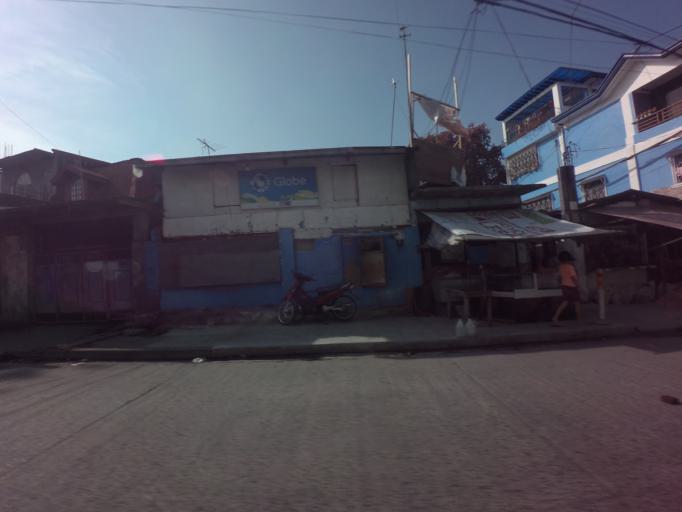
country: PH
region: Calabarzon
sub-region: Province of Rizal
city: Taguig
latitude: 14.4996
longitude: 121.0525
